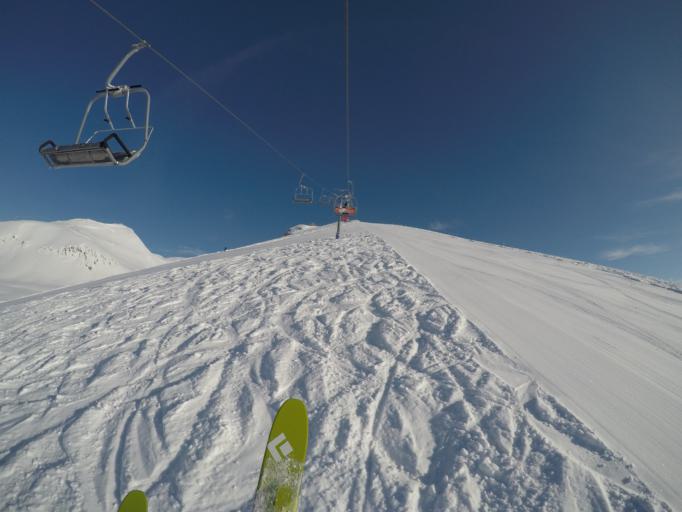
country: GE
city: Gudauri
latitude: 42.4944
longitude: 44.5050
